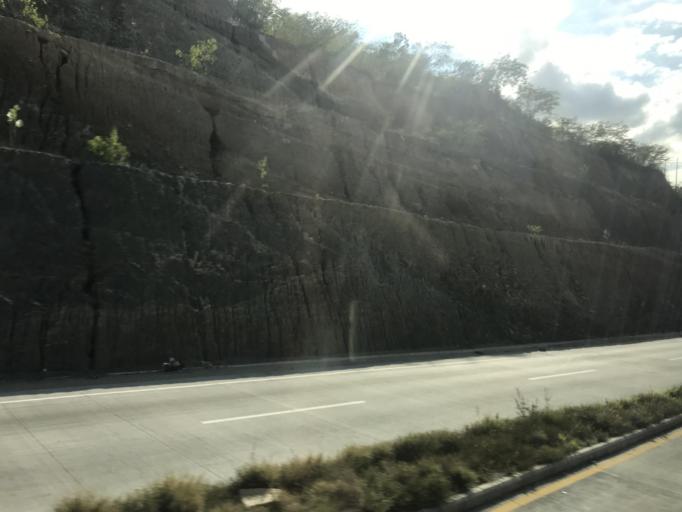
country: GT
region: El Progreso
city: Guastatoya
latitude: 14.8541
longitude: -90.0991
